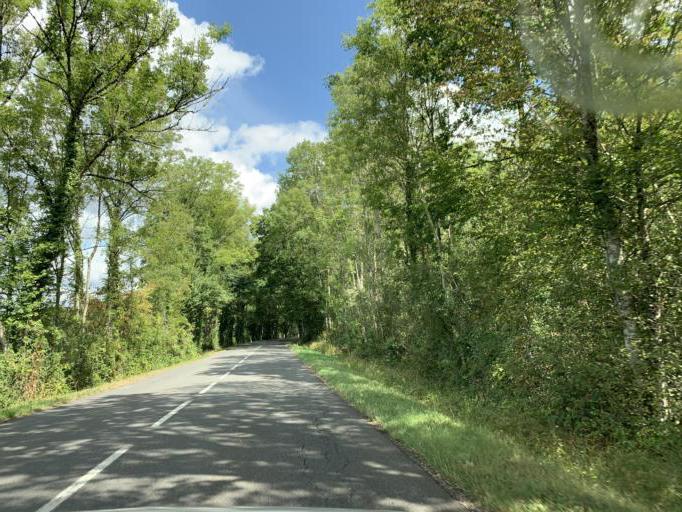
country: FR
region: Bourgogne
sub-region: Departement de l'Yonne
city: Saint-Fargeau
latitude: 47.5951
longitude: 3.1825
